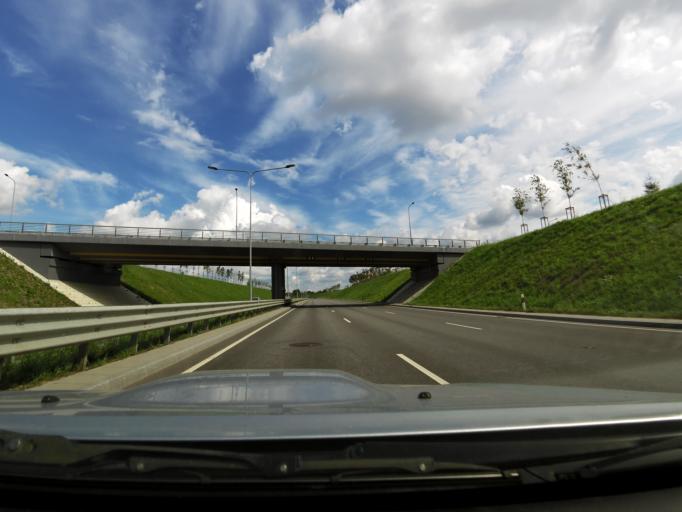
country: LT
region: Vilnius County
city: Pasilaiciai
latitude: 54.7389
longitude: 25.2124
